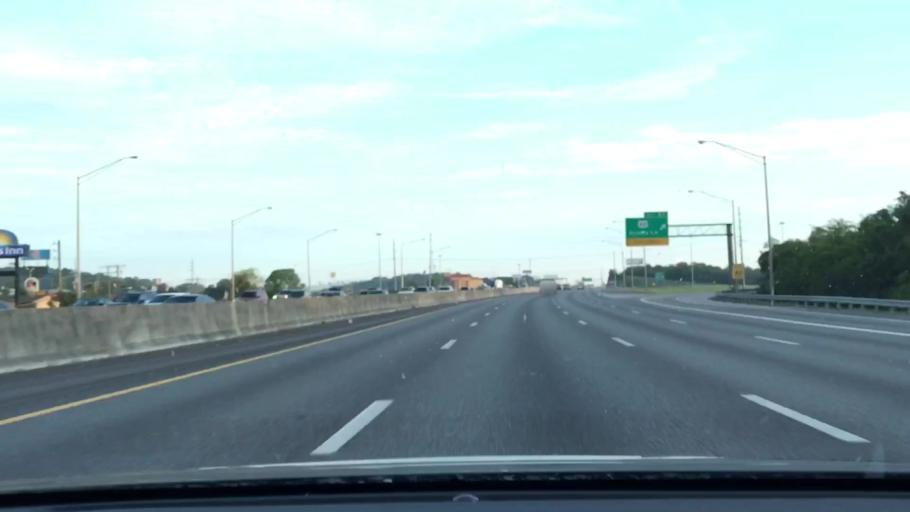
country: US
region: Tennessee
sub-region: Davidson County
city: Nashville
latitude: 36.1960
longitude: -86.7727
